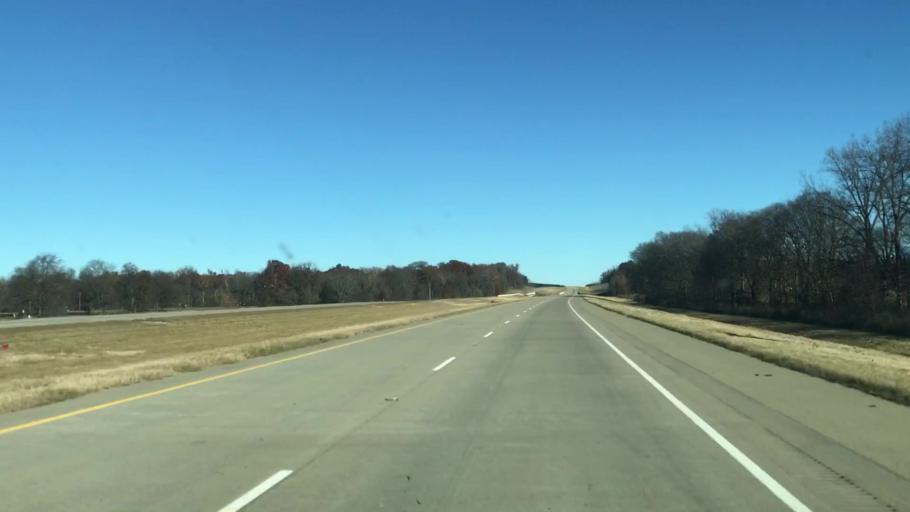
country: US
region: Louisiana
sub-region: Caddo Parish
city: Oil City
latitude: 32.7824
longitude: -93.8889
